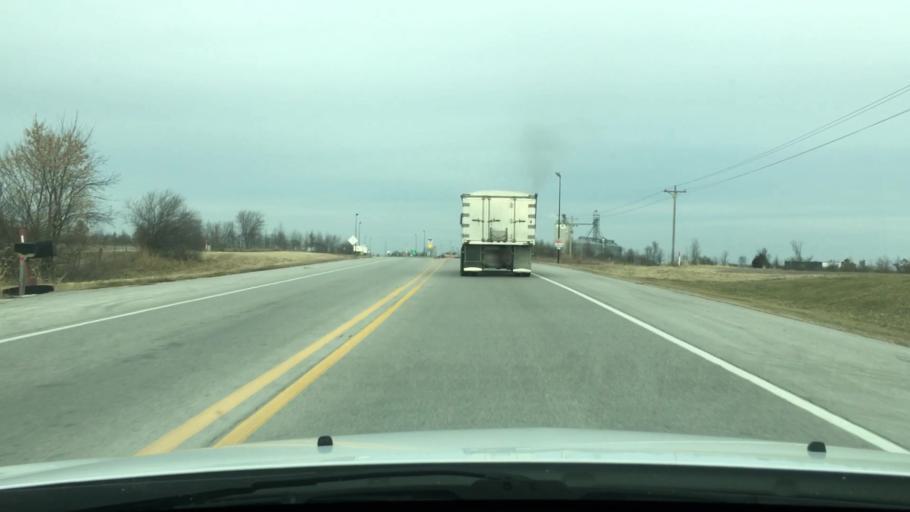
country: US
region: Illinois
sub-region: Pike County
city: Griggsville
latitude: 39.6702
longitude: -90.7695
